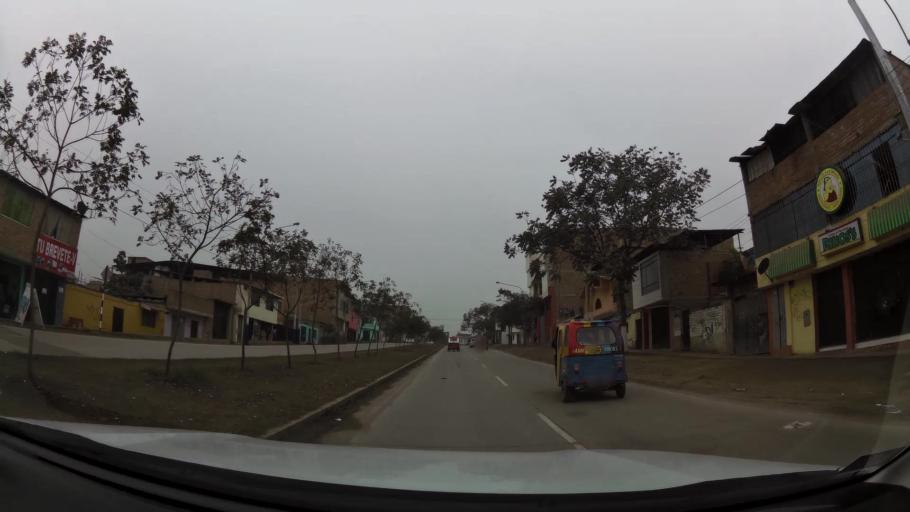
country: PE
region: Lima
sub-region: Lima
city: Surco
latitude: -12.1877
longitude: -76.9251
